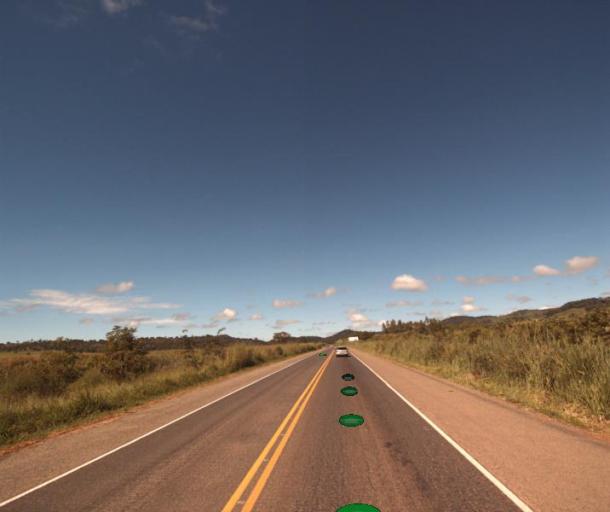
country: BR
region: Goias
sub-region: Ceres
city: Ceres
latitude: -15.2233
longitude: -49.5529
